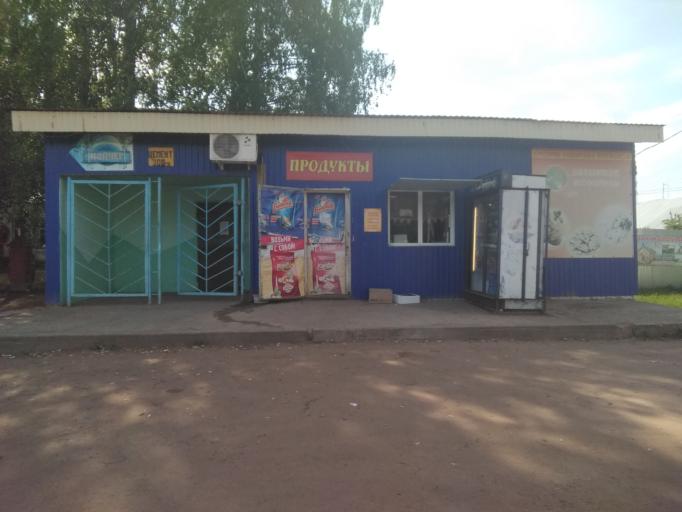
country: RU
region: Bashkortostan
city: Ulukulevo
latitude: 54.4923
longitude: 56.3728
